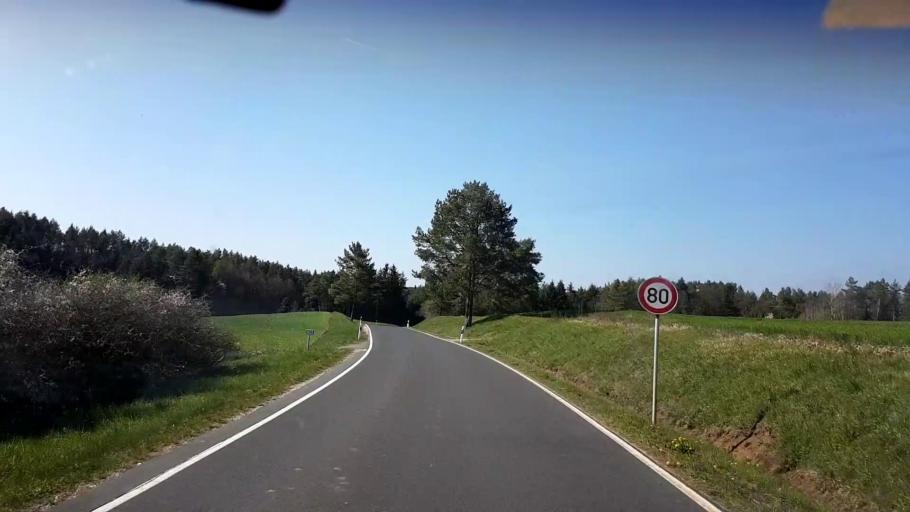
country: DE
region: Bavaria
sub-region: Upper Franconia
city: Waischenfeld
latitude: 49.8043
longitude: 11.3719
